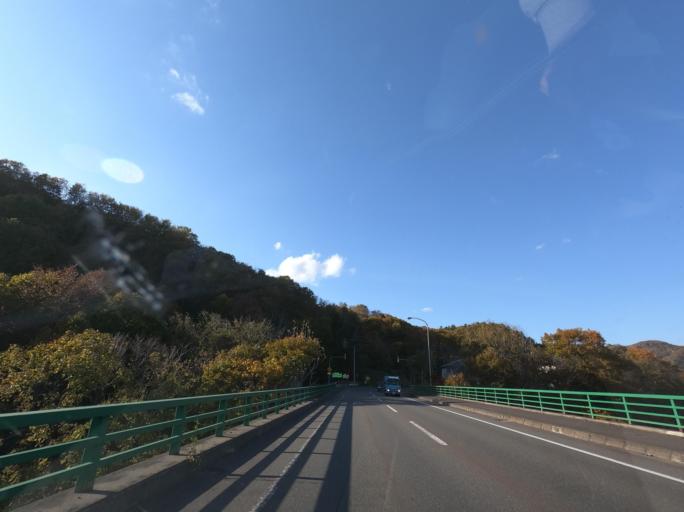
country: JP
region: Hokkaido
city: Iwamizawa
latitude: 42.9993
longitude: 142.0053
